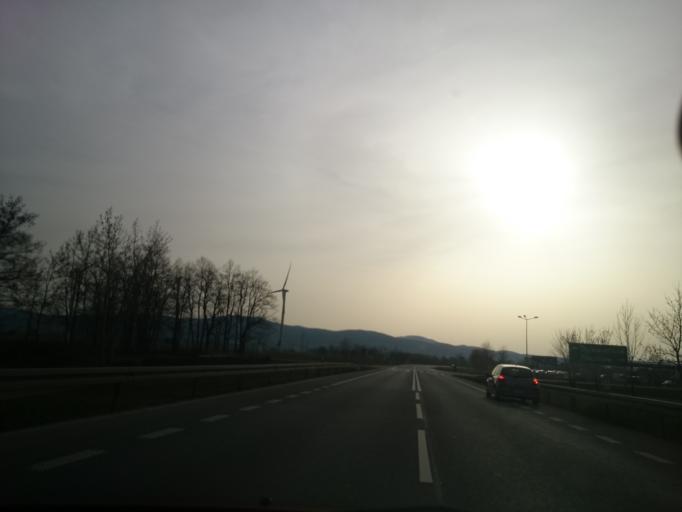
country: PL
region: Opole Voivodeship
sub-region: Powiat nyski
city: Paczkow
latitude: 50.4547
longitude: 17.0147
